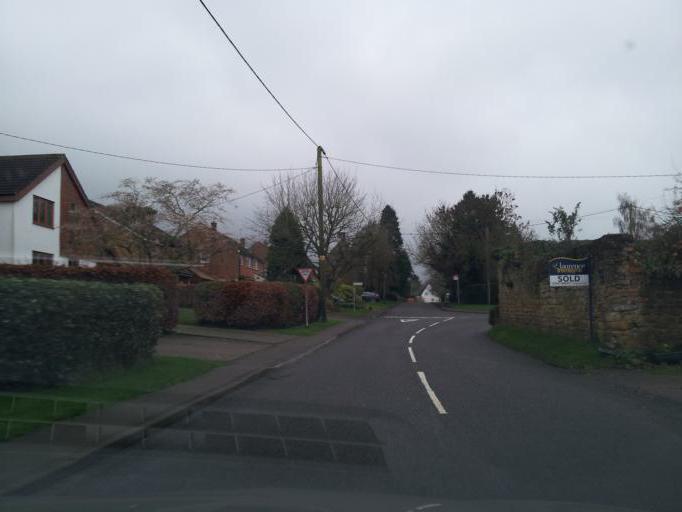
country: GB
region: England
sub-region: Warwickshire
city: Rugby
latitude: 52.3311
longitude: -1.2004
